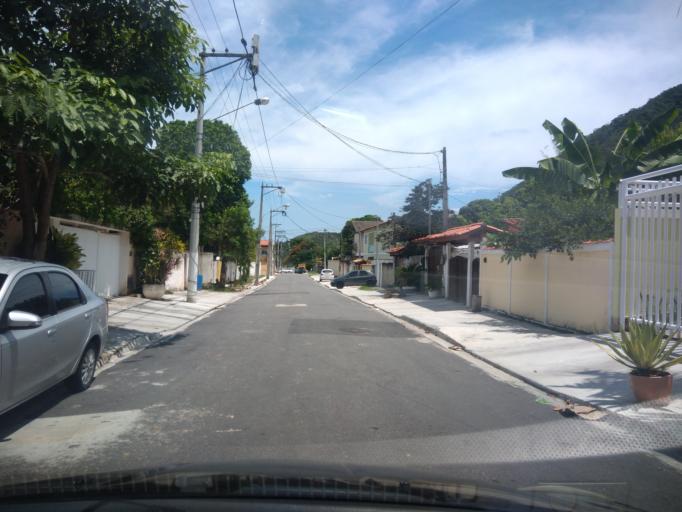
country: BR
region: Rio de Janeiro
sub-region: Niteroi
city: Niteroi
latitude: -22.9286
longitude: -43.0705
